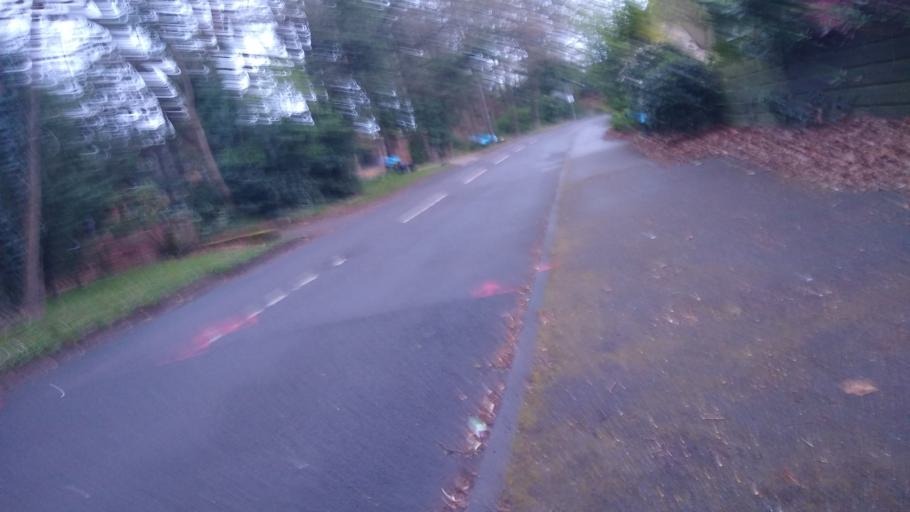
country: GB
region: England
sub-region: Wokingham
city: Winnersh
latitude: 51.4335
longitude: -0.8776
